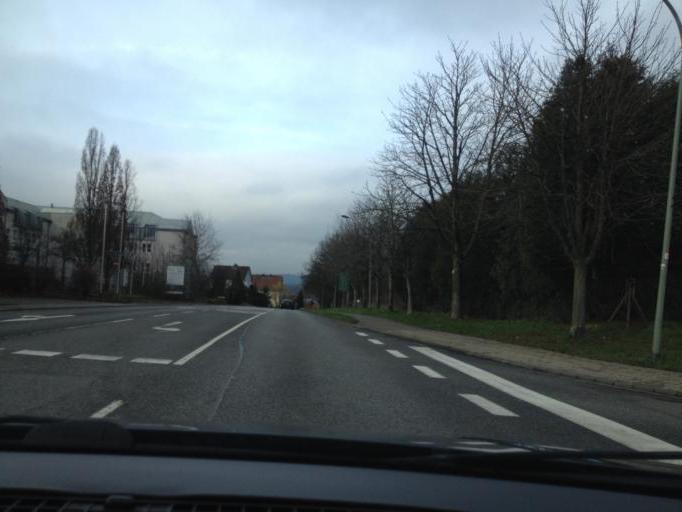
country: DE
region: Saarland
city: Sankt Wendel
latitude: 49.4592
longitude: 7.1766
